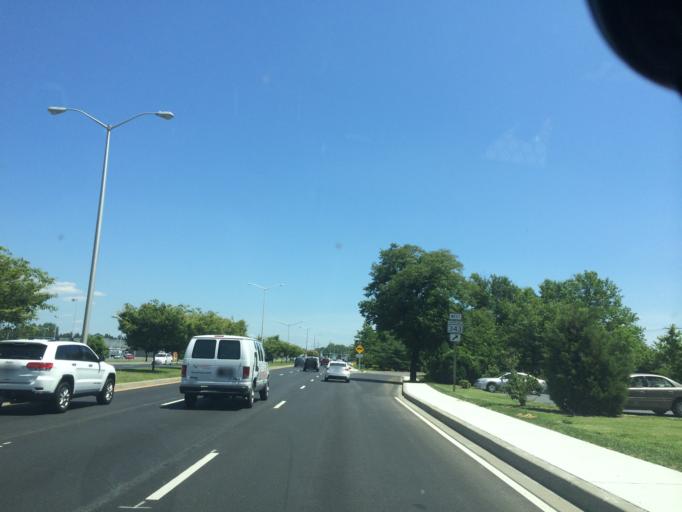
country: US
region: Maryland
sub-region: Dorchester County
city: Cambridge
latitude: 38.5607
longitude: -76.0647
